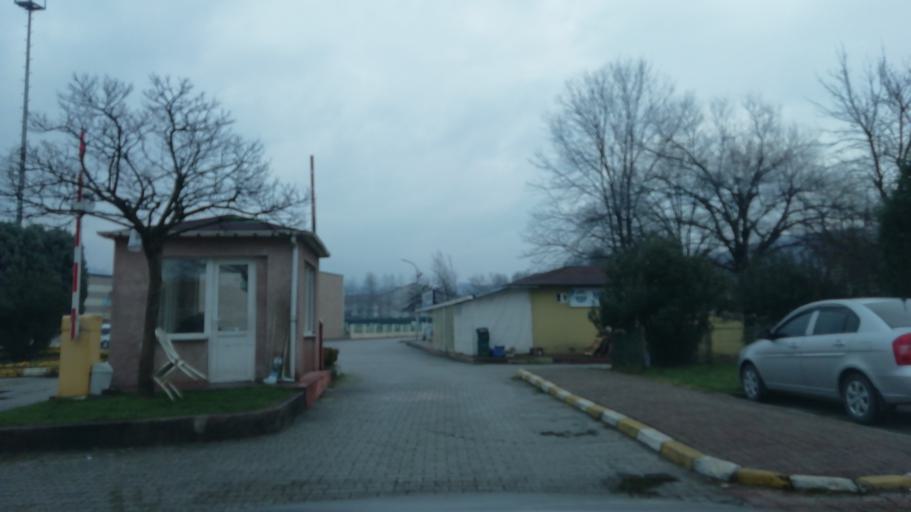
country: TR
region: Sakarya
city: Akyazi
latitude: 40.6261
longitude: 30.6514
